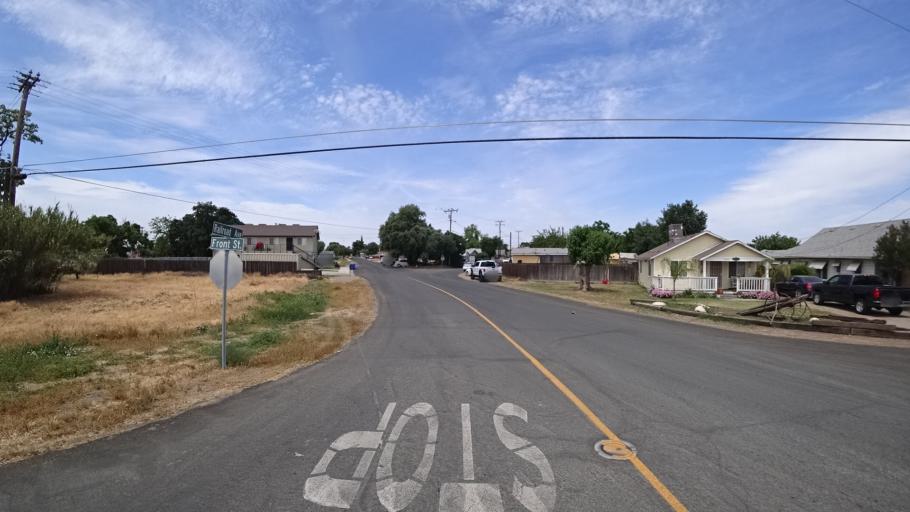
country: US
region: California
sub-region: Kings County
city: Armona
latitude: 36.3163
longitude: -119.7063
